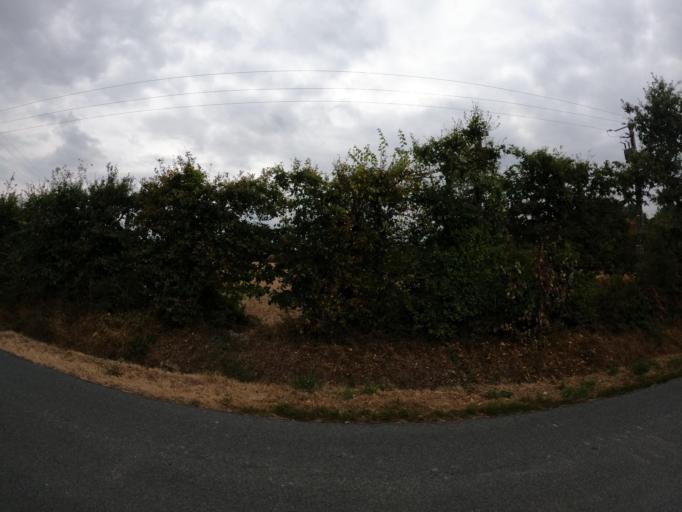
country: FR
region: Pays de la Loire
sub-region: Departement de la Vendee
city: Tiffauges
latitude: 47.0013
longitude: -1.0951
